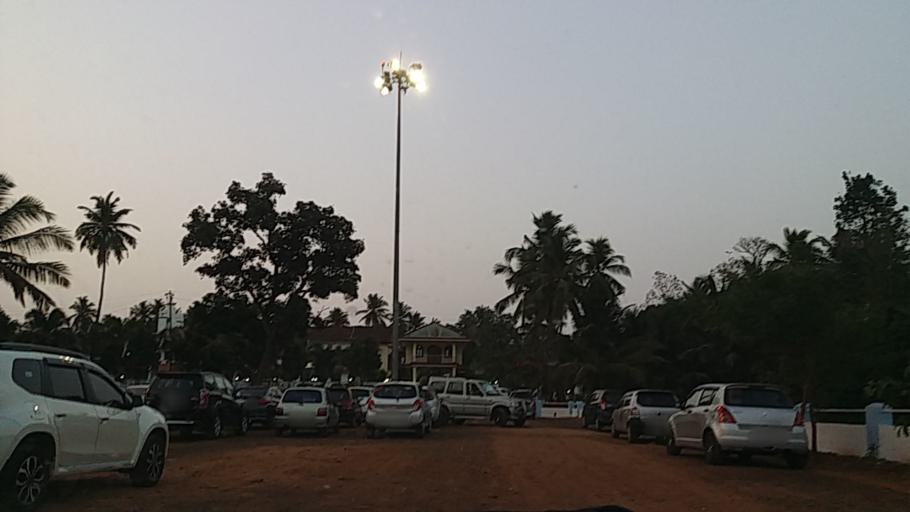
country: IN
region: Goa
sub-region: South Goa
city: Chinchinim
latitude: 15.2161
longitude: 73.9694
